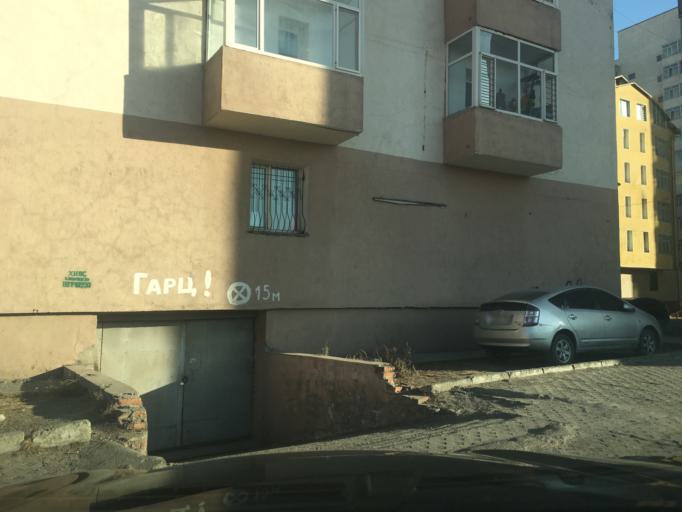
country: MN
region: Ulaanbaatar
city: Ulaanbaatar
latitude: 47.9157
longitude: 106.8742
